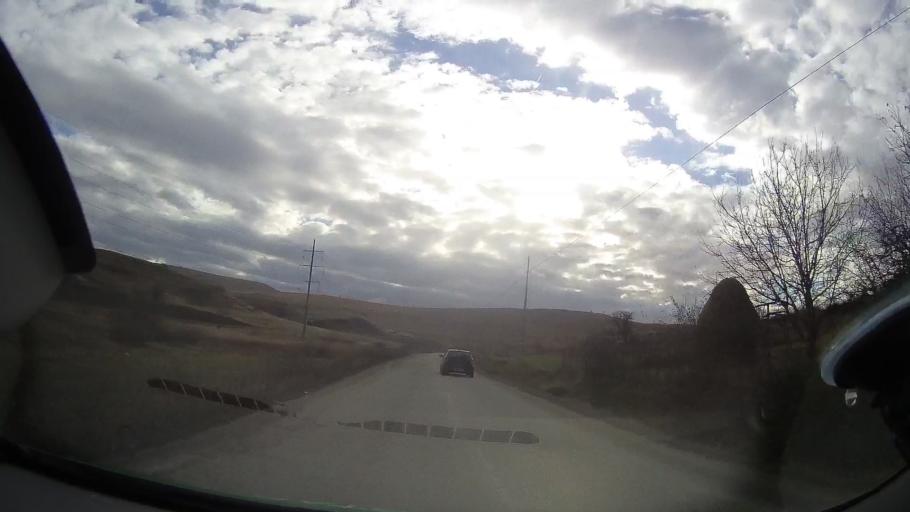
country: RO
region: Cluj
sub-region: Comuna Baisoara
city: Baisoara
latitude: 46.5995
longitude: 23.4631
